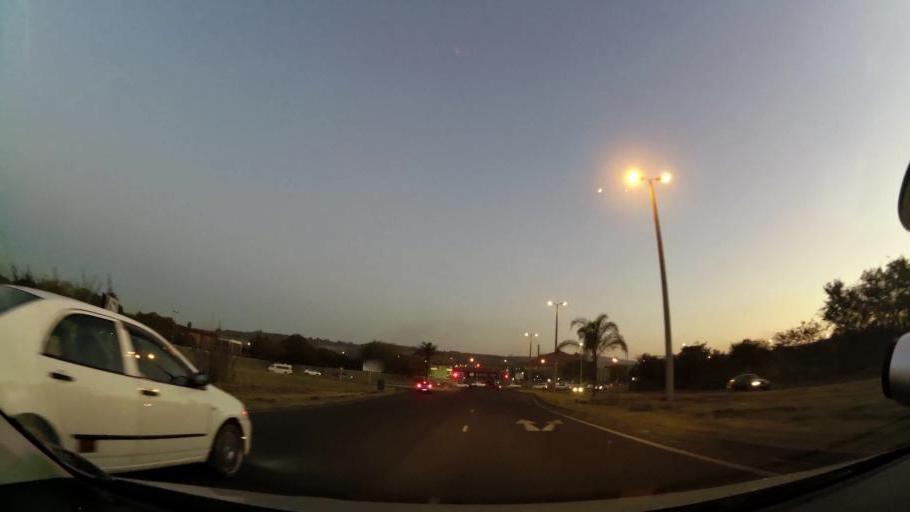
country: ZA
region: Gauteng
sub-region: City of Tshwane Metropolitan Municipality
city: Pretoria
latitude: -25.7606
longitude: 28.1331
